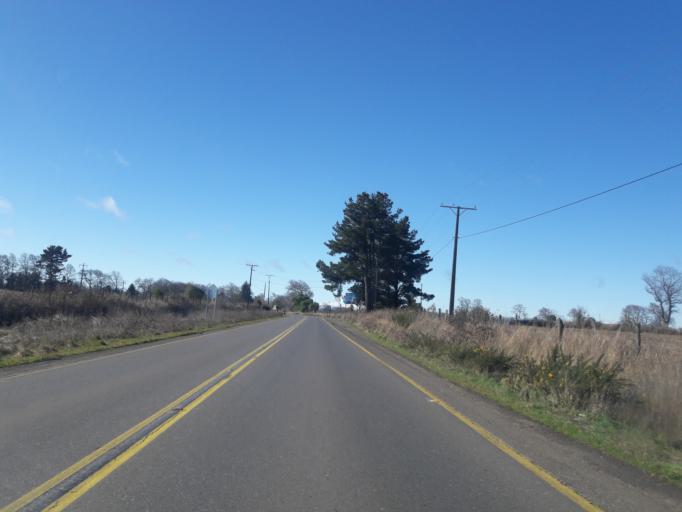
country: CL
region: Araucania
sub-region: Provincia de Malleco
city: Victoria
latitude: -38.2536
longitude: -72.2906
